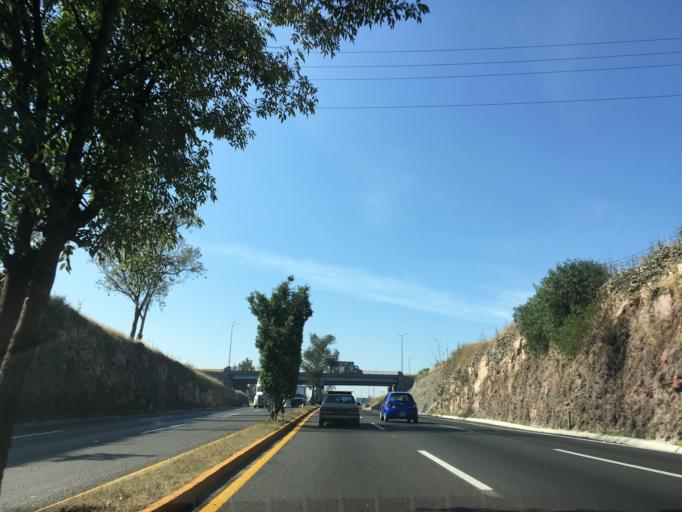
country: MX
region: Michoacan
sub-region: Tarimbaro
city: San Bernabe de las Canteras
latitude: 19.7600
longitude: -101.1669
